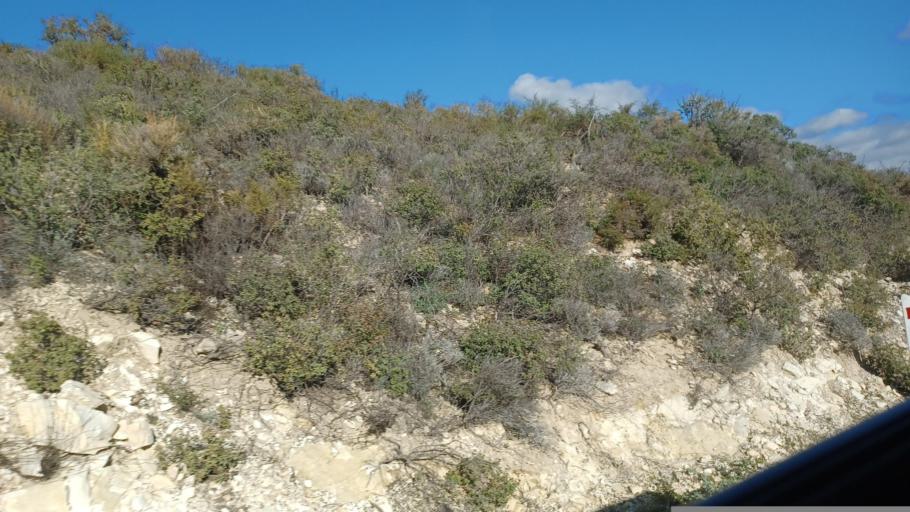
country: CY
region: Limassol
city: Pachna
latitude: 34.8390
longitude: 32.8034
